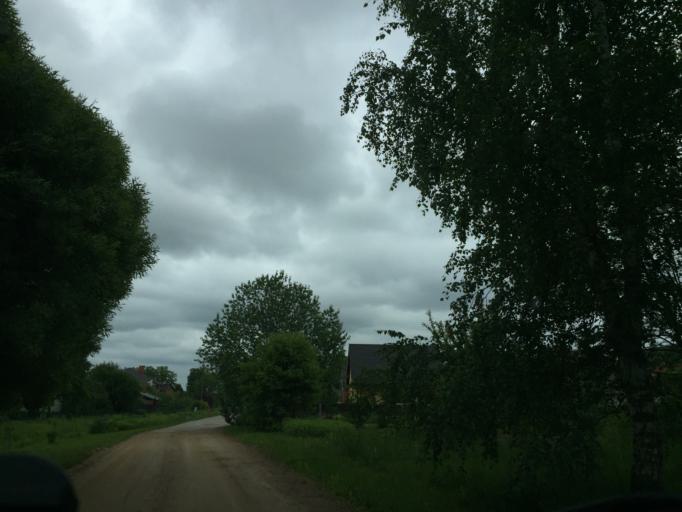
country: LV
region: Valmieras Rajons
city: Valmiera
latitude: 57.5547
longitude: 25.4183
